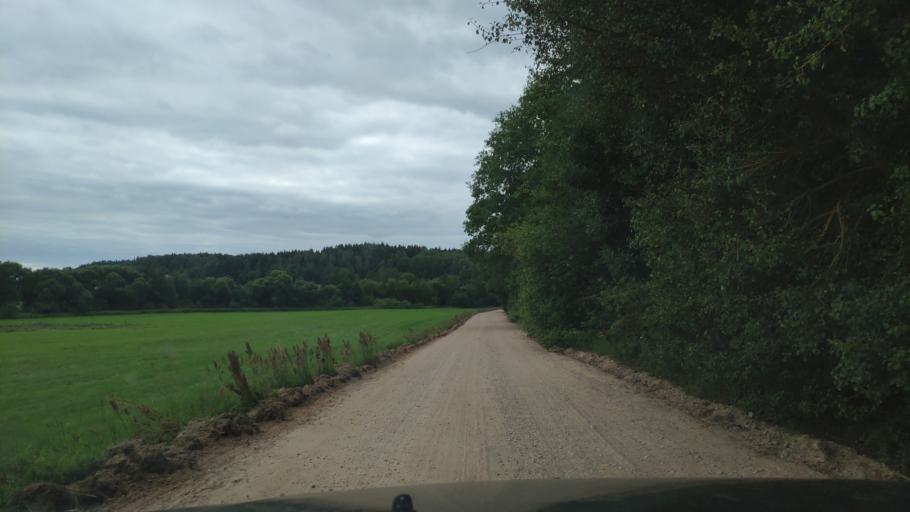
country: BY
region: Minsk
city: Khatsyezhyna
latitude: 53.9353
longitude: 27.2763
